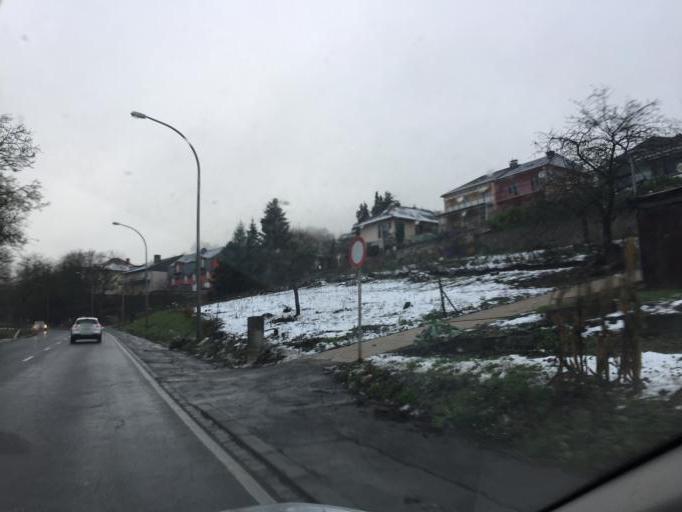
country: LU
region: Diekirch
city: Warken
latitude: 49.8501
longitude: 6.0770
